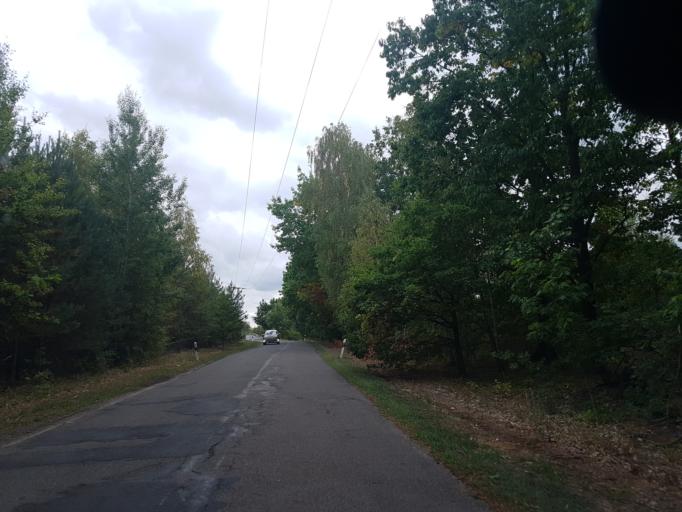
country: DE
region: Saxony-Anhalt
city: Rosslau
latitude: 51.9640
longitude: 12.3001
